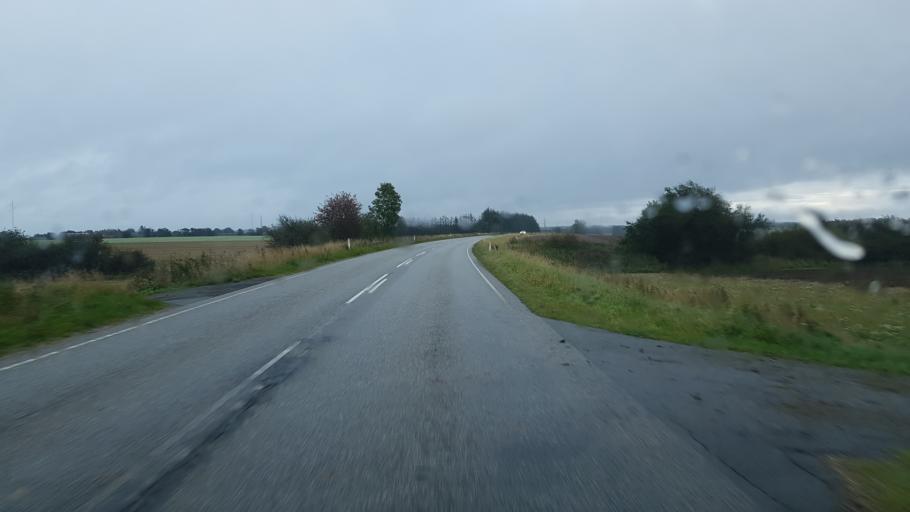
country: DK
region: South Denmark
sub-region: Kolding Kommune
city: Vamdrup
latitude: 55.3425
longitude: 9.2792
